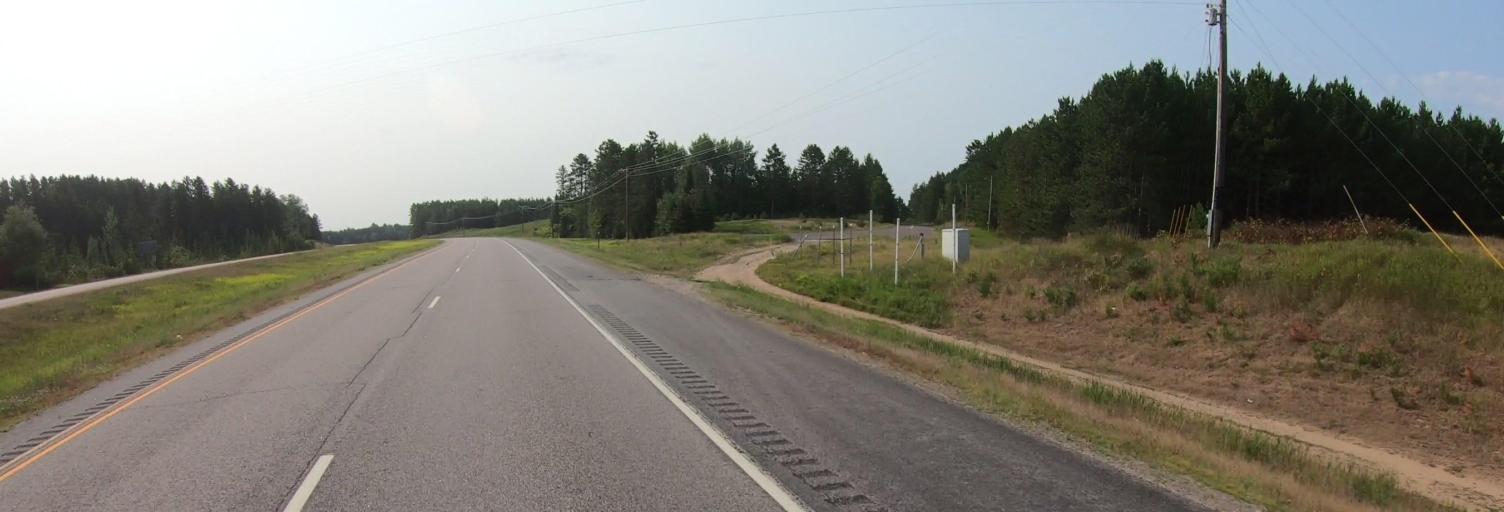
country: US
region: Minnesota
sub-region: Saint Louis County
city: Mountain Iron
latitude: 47.6713
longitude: -92.6476
